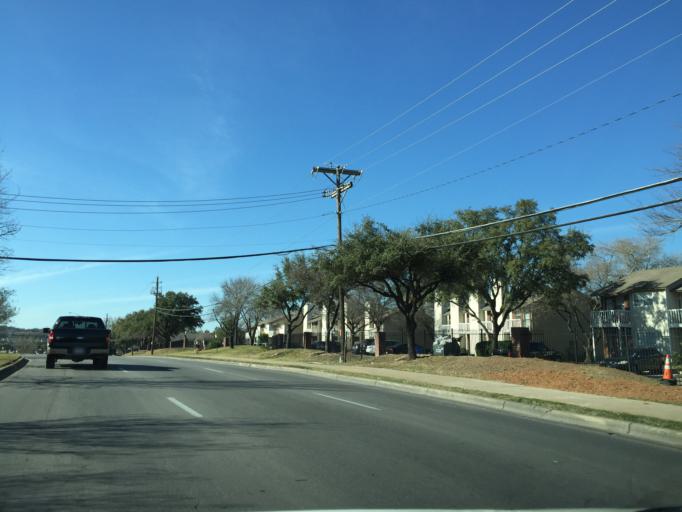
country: US
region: Texas
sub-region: Travis County
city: Austin
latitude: 30.2299
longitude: -97.7132
